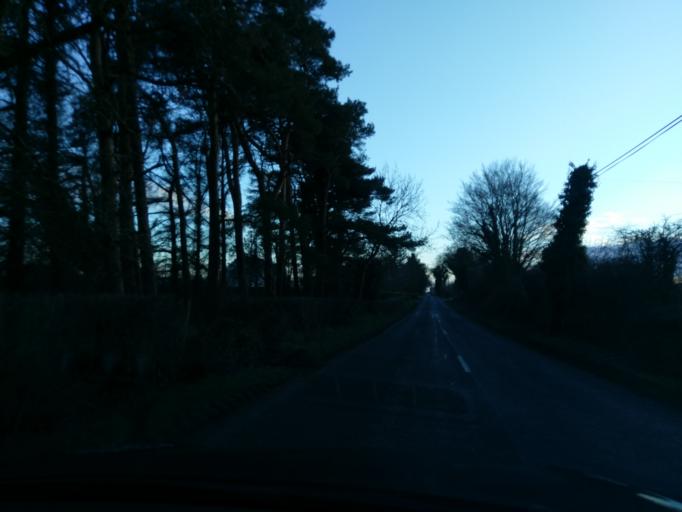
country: IE
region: Connaught
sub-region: County Galway
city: Athenry
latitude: 53.3013
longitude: -8.6255
